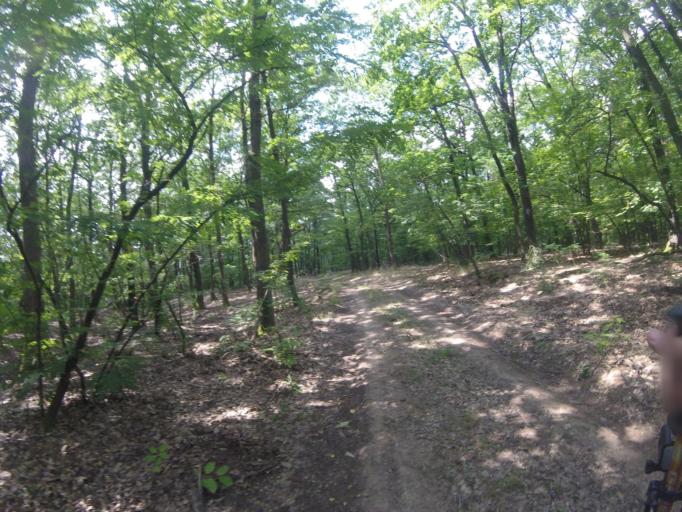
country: SK
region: Nitriansky
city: Sahy
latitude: 48.0266
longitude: 18.9265
